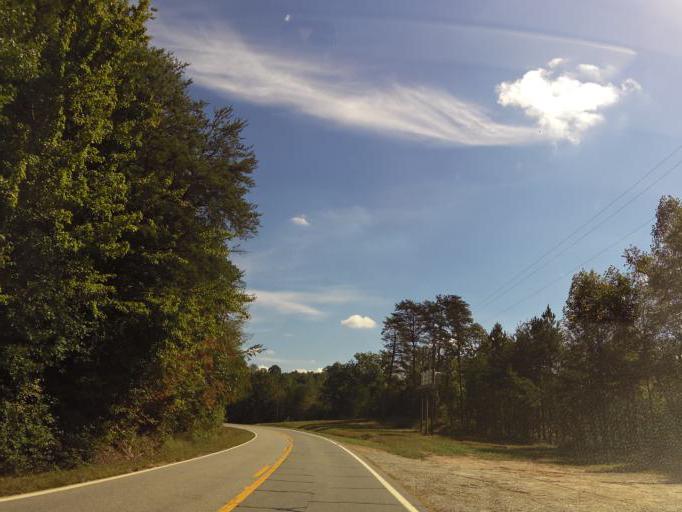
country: US
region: Georgia
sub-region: Dawson County
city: Dawsonville
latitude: 34.5235
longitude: -84.2570
